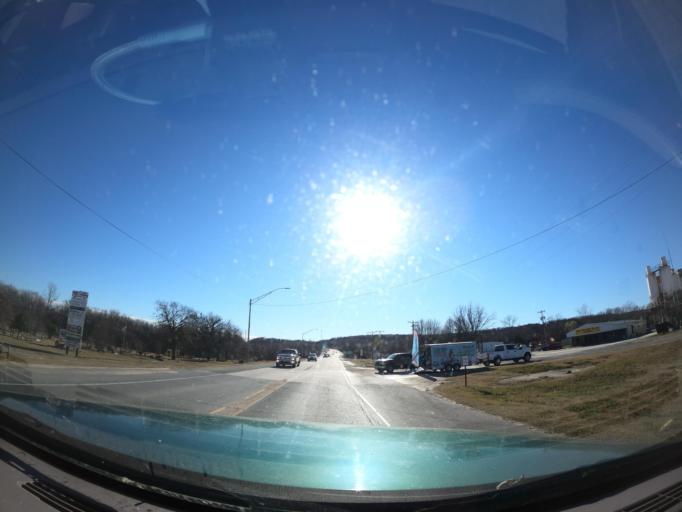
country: US
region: Oklahoma
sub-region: McIntosh County
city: Eufaula
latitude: 35.2774
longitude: -95.5839
